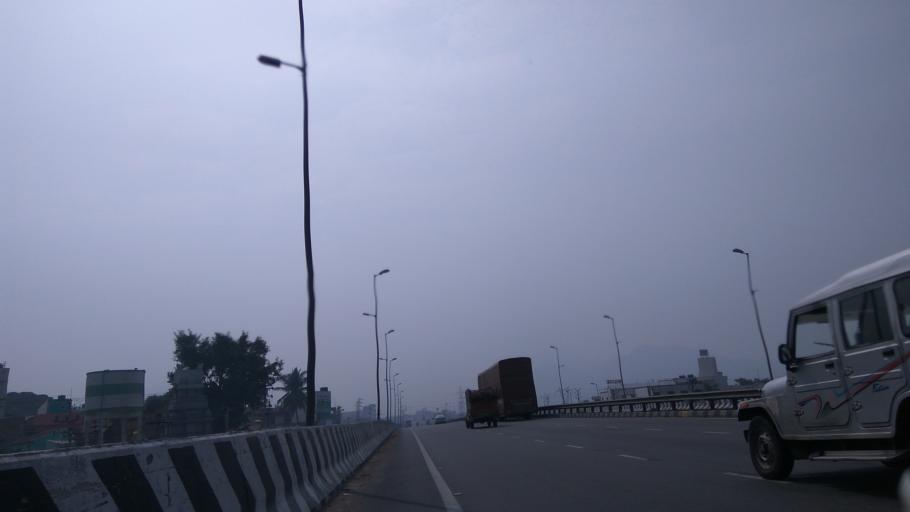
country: IN
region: Tamil Nadu
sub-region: Krishnagiri
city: Krishnagiri
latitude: 12.5146
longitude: 78.2169
